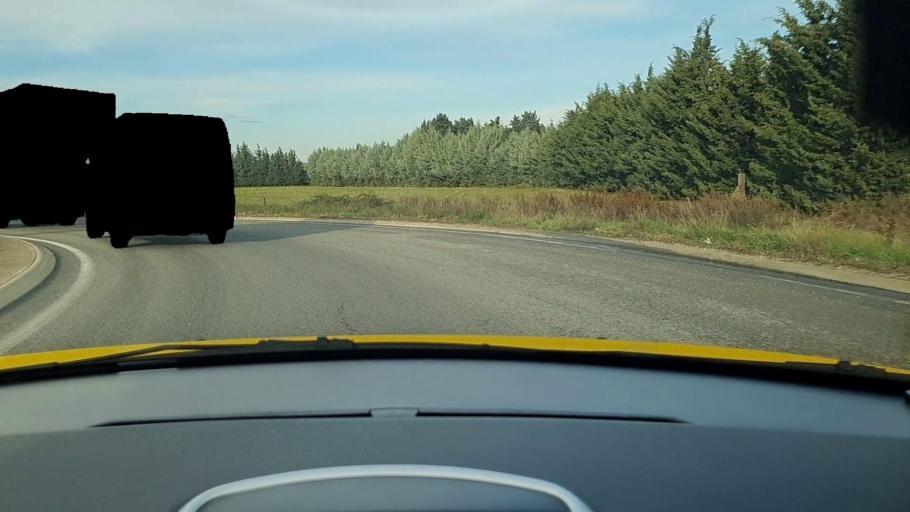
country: FR
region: Languedoc-Roussillon
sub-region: Departement du Gard
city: Beaucaire
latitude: 43.7914
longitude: 4.6364
